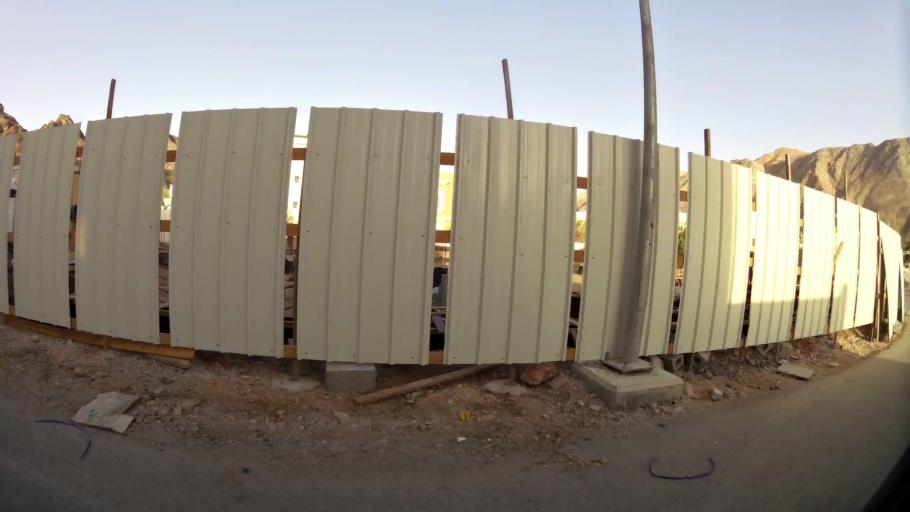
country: OM
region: Muhafazat Masqat
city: Muscat
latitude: 23.5682
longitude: 58.5785
